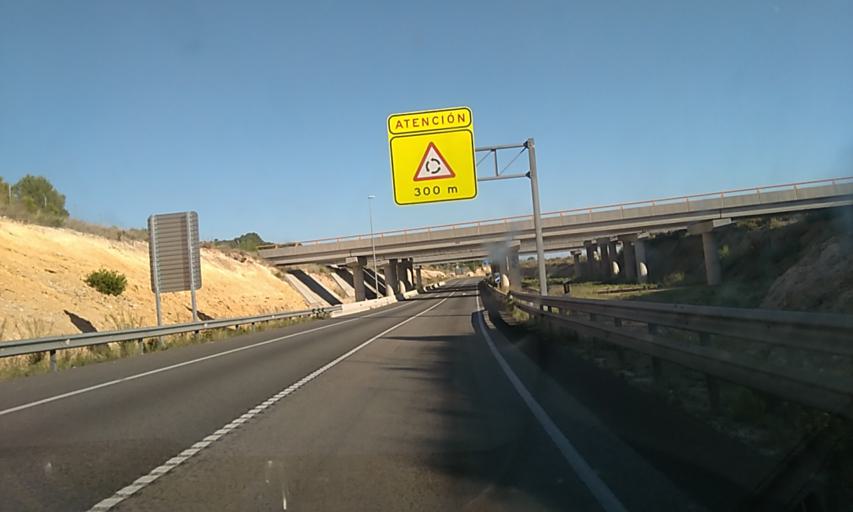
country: ES
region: Valencia
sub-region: Provincia de Castello
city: Torreblanca
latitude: 40.2314
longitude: 0.2082
